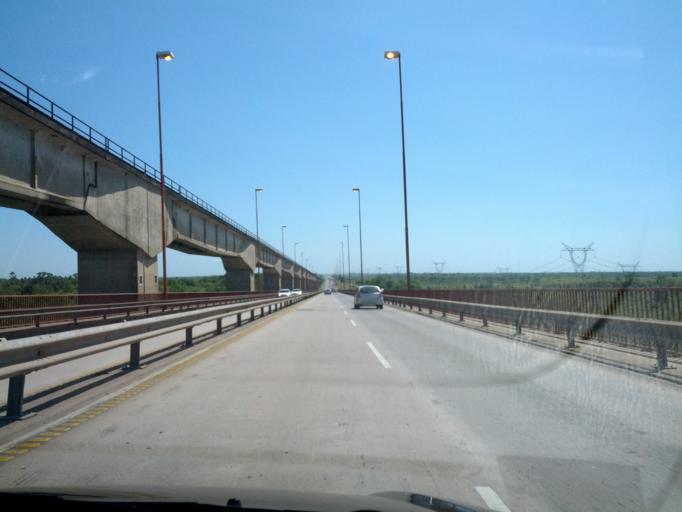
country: AR
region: Buenos Aires
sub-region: Partido de Zarate
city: Zarate
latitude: -34.0924
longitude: -58.9994
